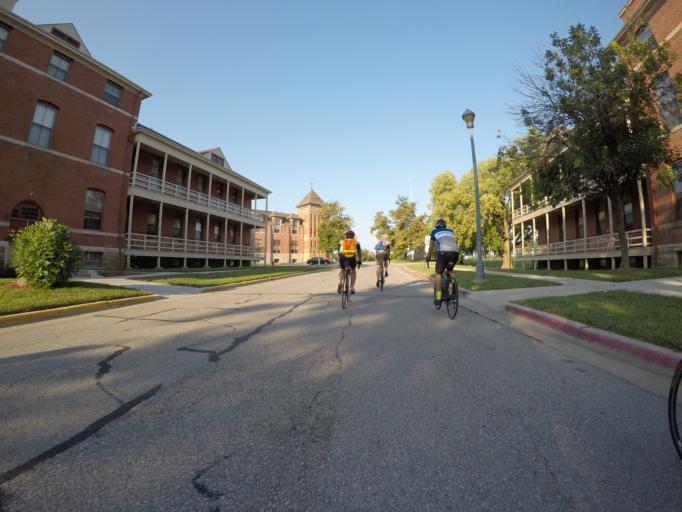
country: US
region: Kansas
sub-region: Leavenworth County
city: Lansing
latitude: 39.2806
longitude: -94.8951
